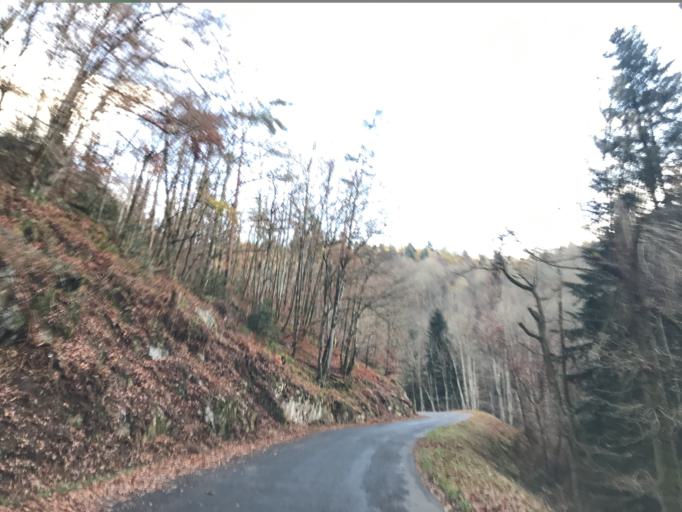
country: FR
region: Auvergne
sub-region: Departement du Puy-de-Dome
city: Courpiere
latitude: 45.7593
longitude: 3.6288
